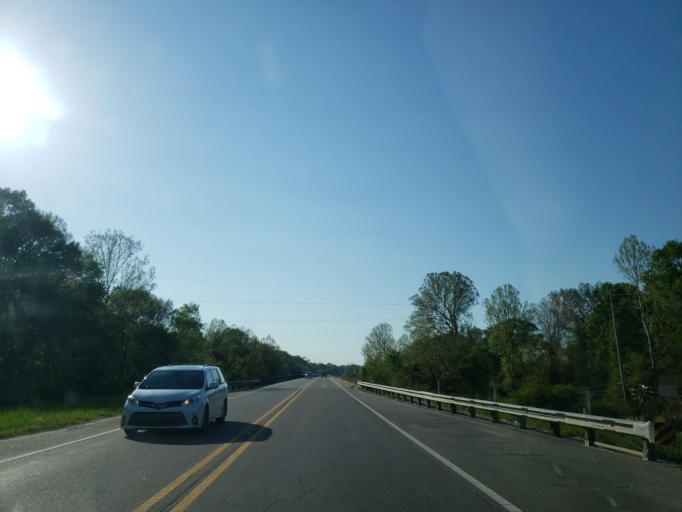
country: US
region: Mississippi
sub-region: Jones County
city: Laurel
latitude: 31.6803
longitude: -89.1143
